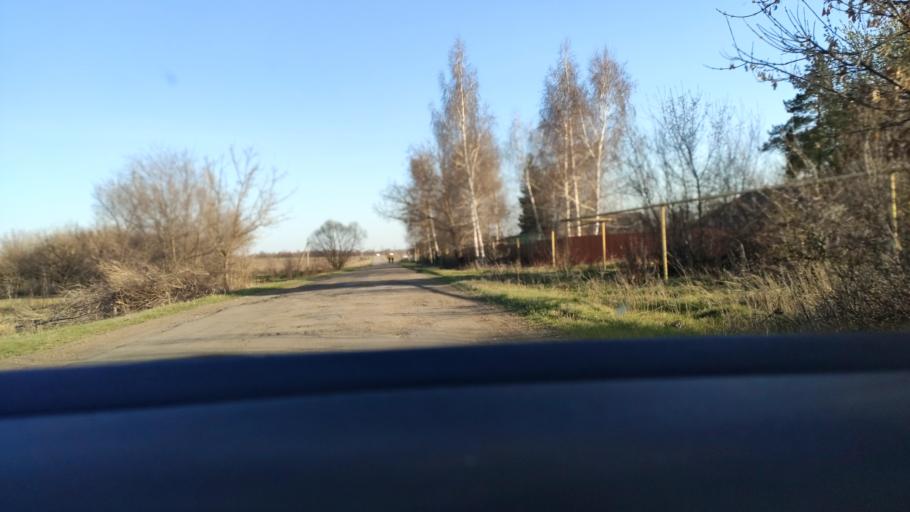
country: RU
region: Voronezj
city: Uryv-Pokrovka
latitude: 51.1390
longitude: 39.0409
